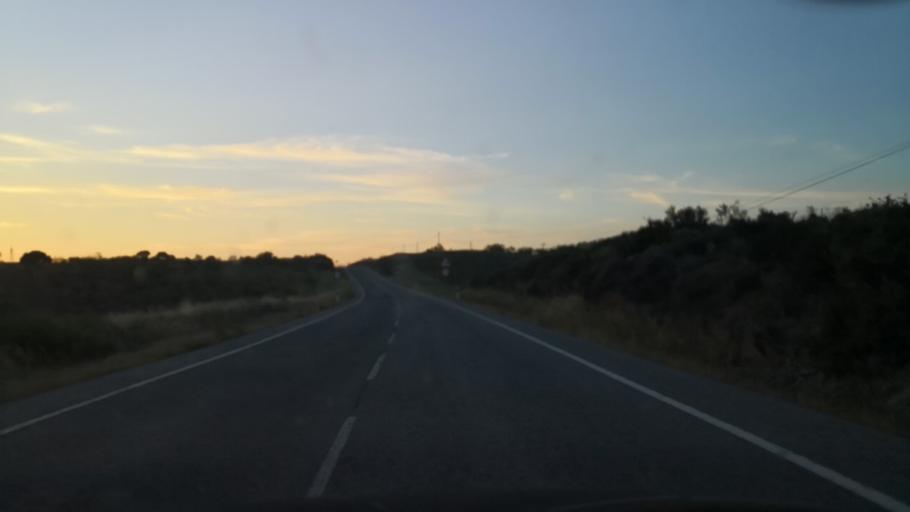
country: ES
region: Extremadura
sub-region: Provincia de Caceres
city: Alcantara
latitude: 39.6927
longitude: -6.8687
